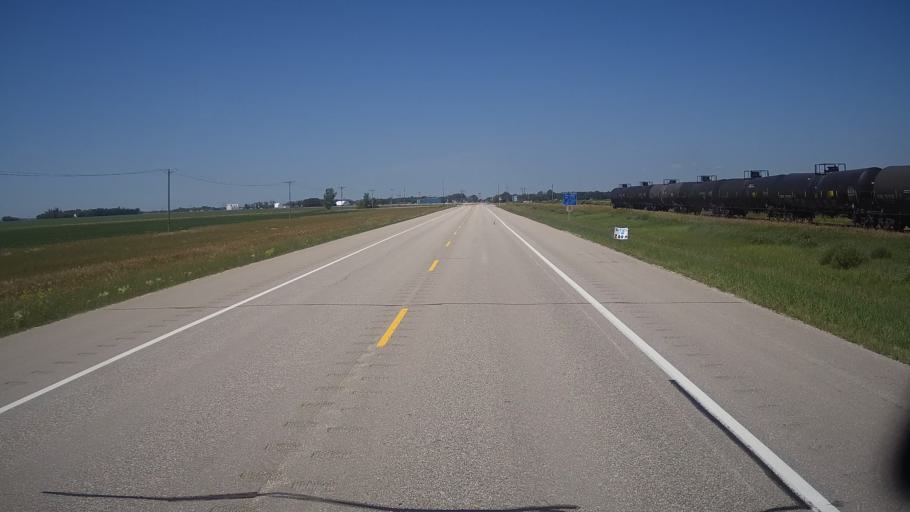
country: CA
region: Manitoba
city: Stonewall
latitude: 50.1172
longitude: -97.5236
